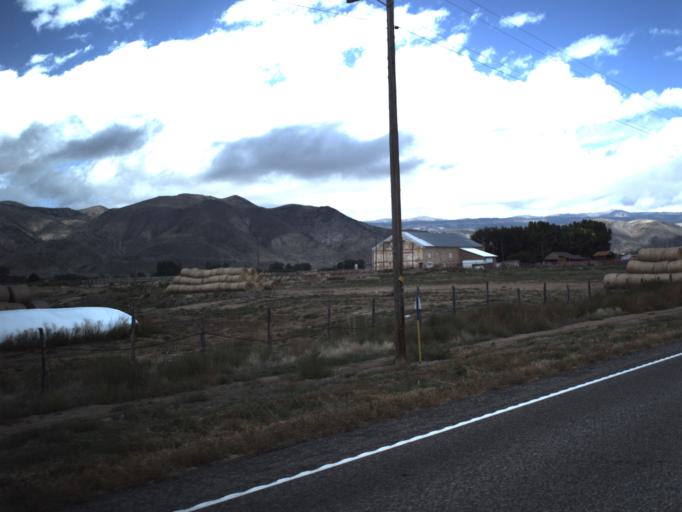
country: US
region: Utah
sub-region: Sevier County
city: Monroe
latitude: 38.6786
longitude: -112.1214
